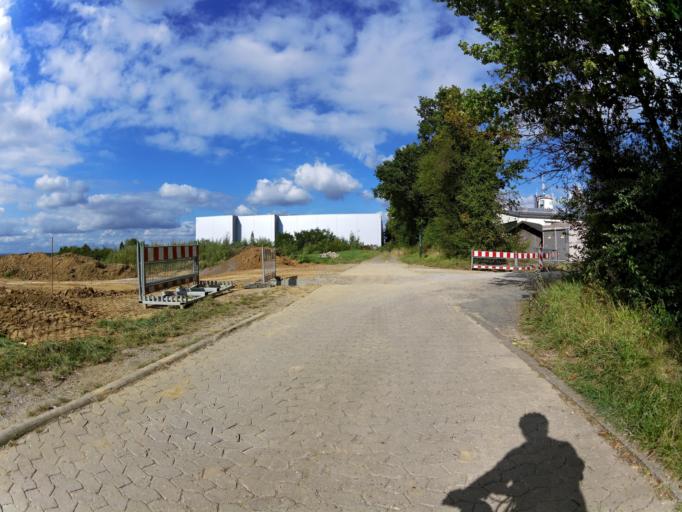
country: DE
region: Bavaria
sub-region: Regierungsbezirk Unterfranken
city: Waldbuttelbrunn
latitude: 49.7920
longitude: 9.8430
